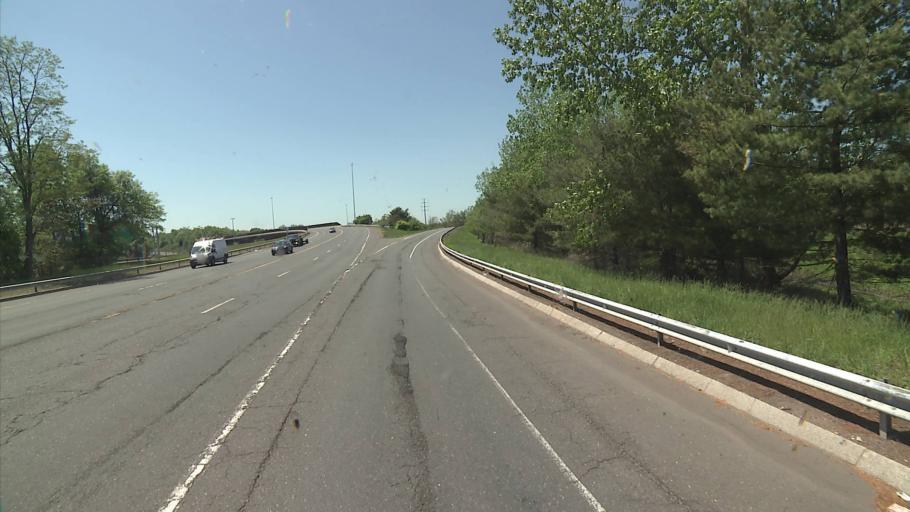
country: US
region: Connecticut
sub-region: Hartford County
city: East Hartford
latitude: 41.7672
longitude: -72.6237
